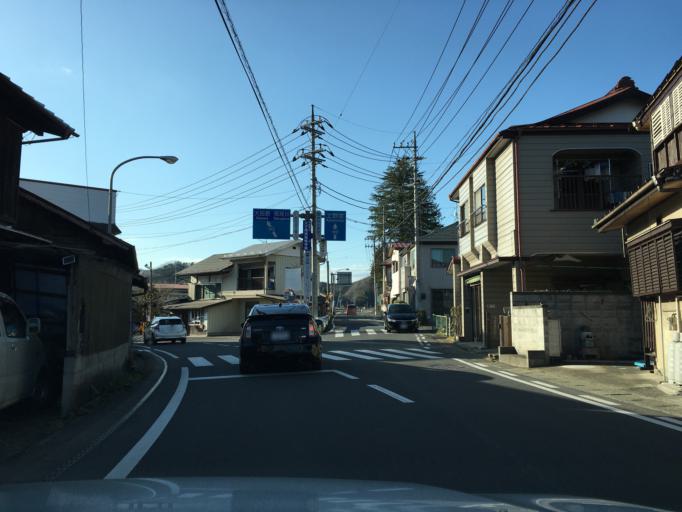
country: JP
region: Ibaraki
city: Daigo
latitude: 36.7756
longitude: 140.3478
